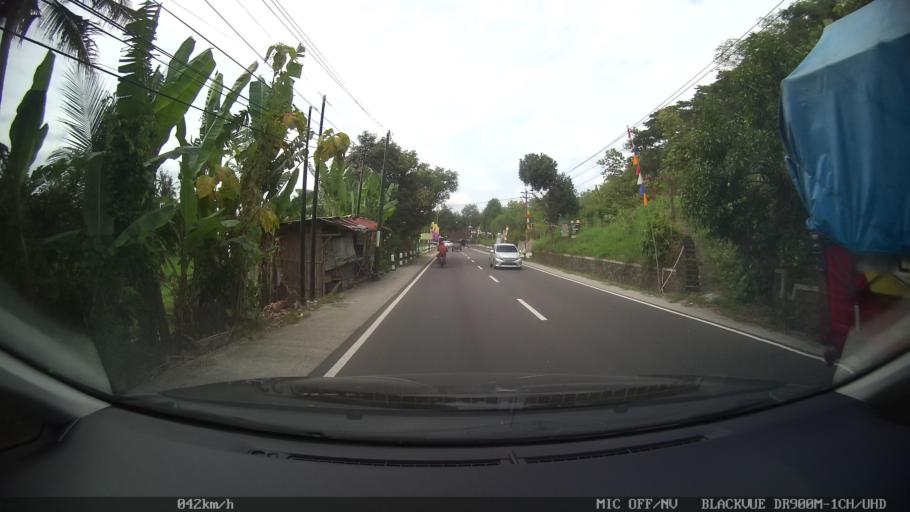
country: ID
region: Central Java
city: Candi Prambanan
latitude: -7.7687
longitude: 110.4866
